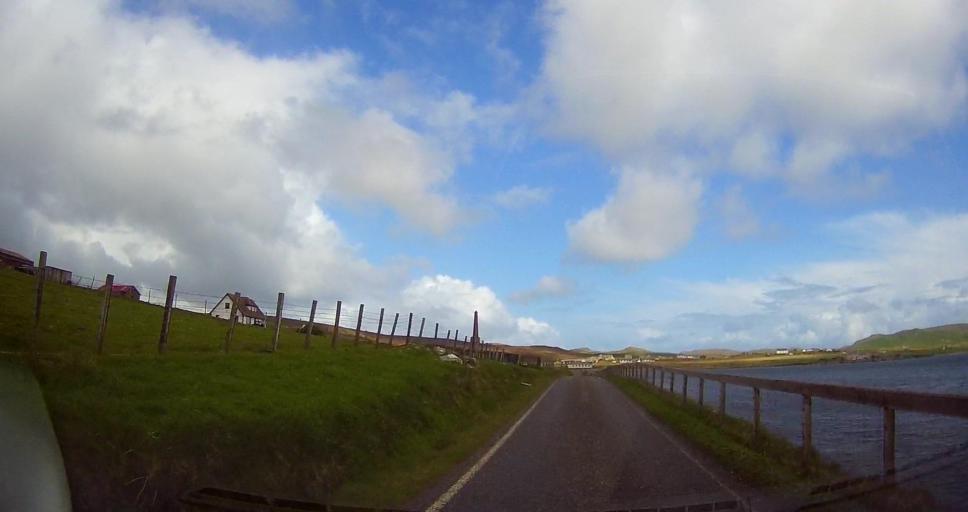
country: GB
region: Scotland
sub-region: Shetland Islands
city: Lerwick
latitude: 60.5799
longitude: -1.3328
